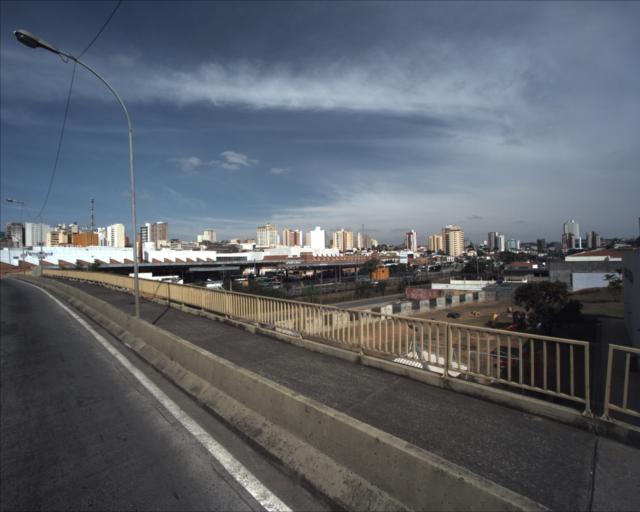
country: BR
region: Sao Paulo
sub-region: Sorocaba
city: Sorocaba
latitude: -23.4945
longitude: -47.4591
